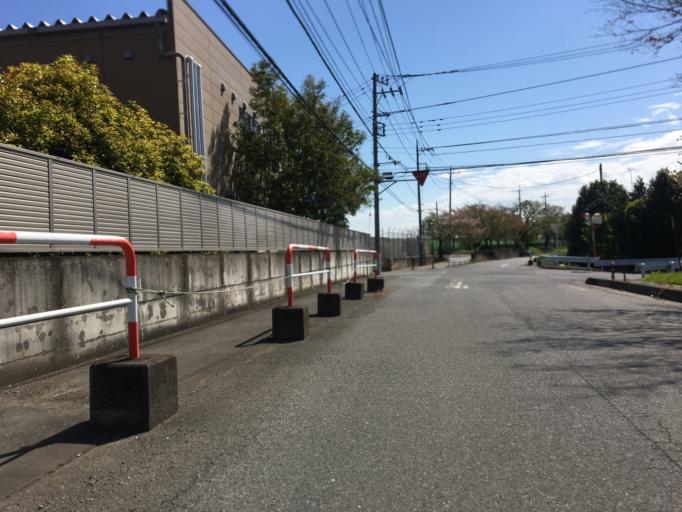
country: JP
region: Saitama
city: Wako
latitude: 35.8036
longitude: 139.6271
